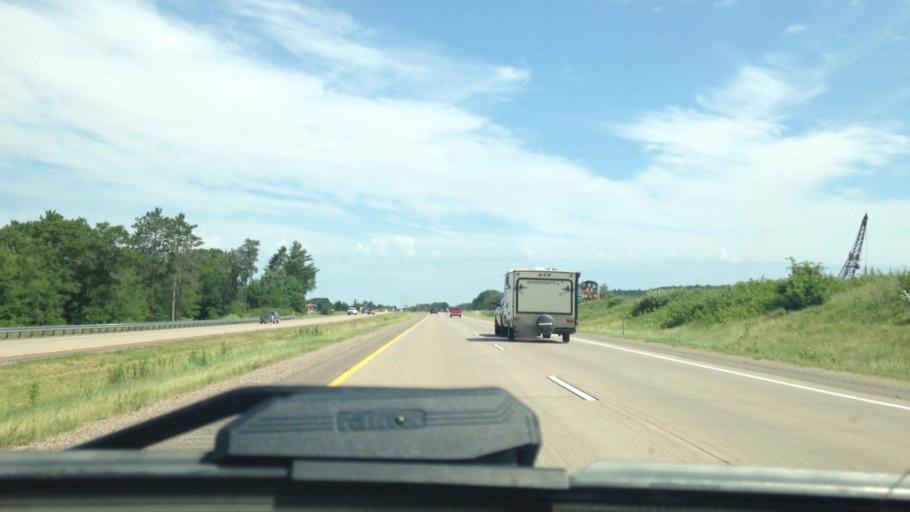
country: US
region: Wisconsin
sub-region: Washburn County
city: Spooner
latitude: 45.8754
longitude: -91.8295
